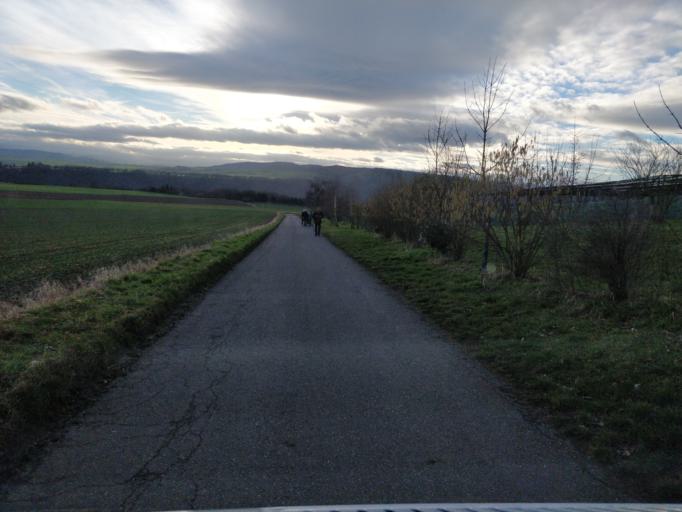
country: DE
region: Rheinland-Pfalz
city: Leutesdorf
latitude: 50.4597
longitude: 7.3991
